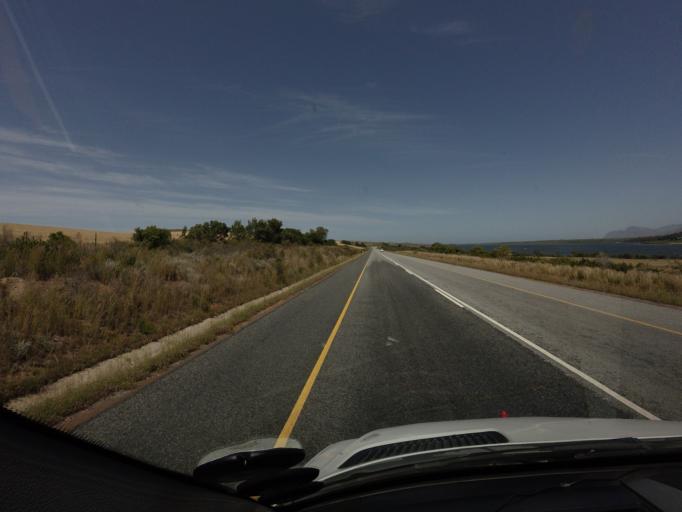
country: ZA
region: Western Cape
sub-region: Overberg District Municipality
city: Hermanus
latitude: -34.3201
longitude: 19.1465
